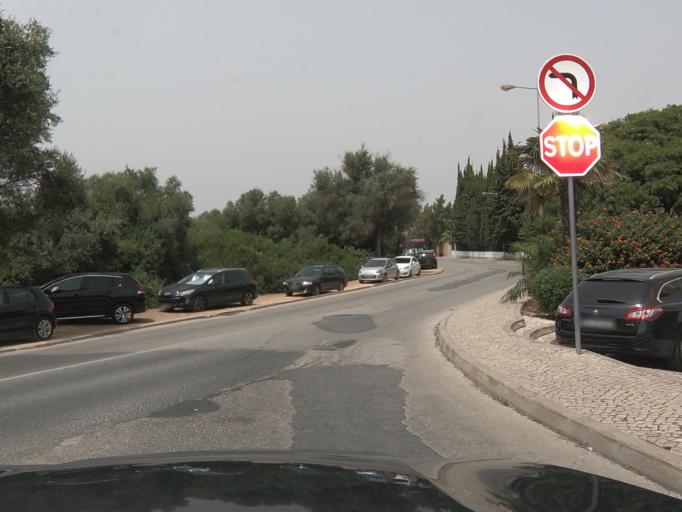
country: PT
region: Faro
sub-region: Portimao
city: Portimao
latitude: 37.1222
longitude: -8.5403
